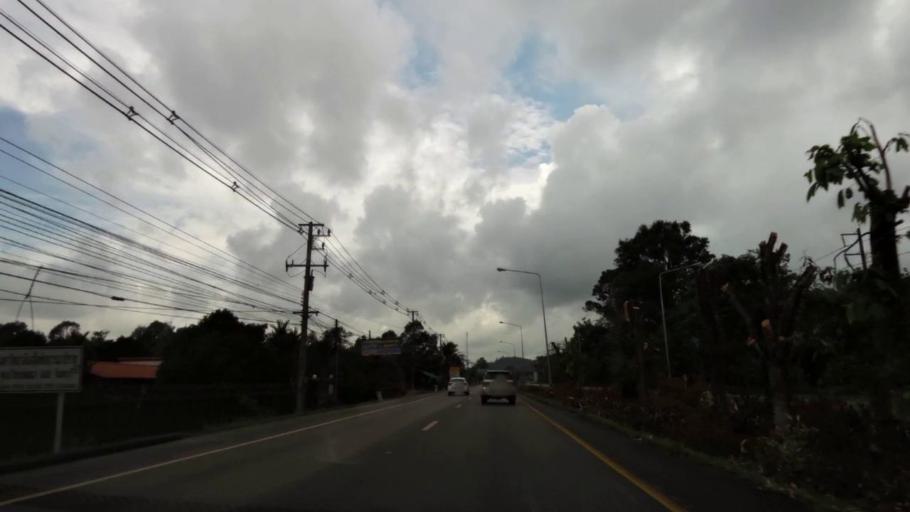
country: TH
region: Chanthaburi
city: Khlung
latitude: 12.5046
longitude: 102.1699
